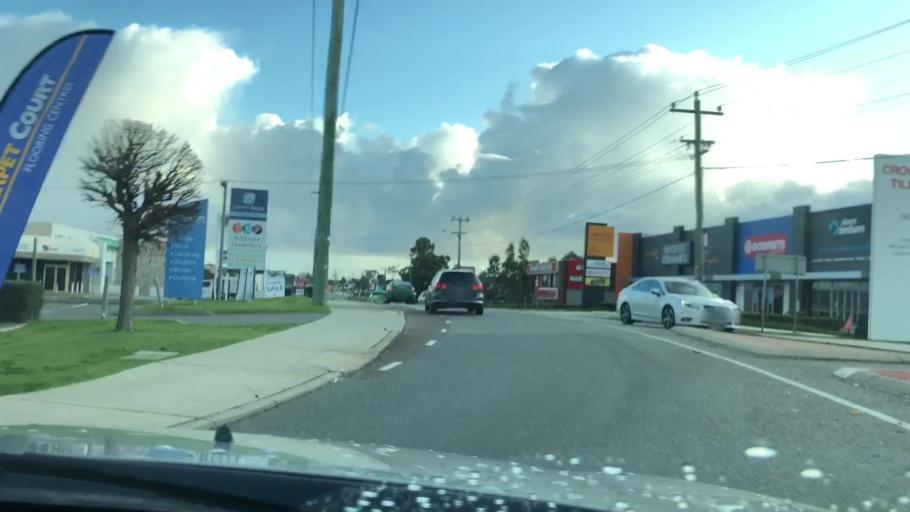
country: AU
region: Western Australia
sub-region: Melville
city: Myaree
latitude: -32.0436
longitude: 115.8222
